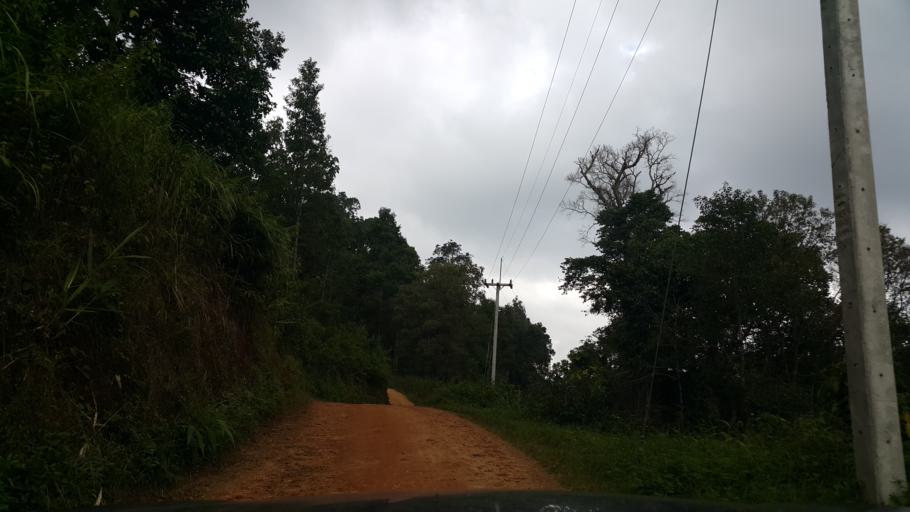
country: TH
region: Lampang
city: Wang Nuea
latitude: 19.1148
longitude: 99.3647
